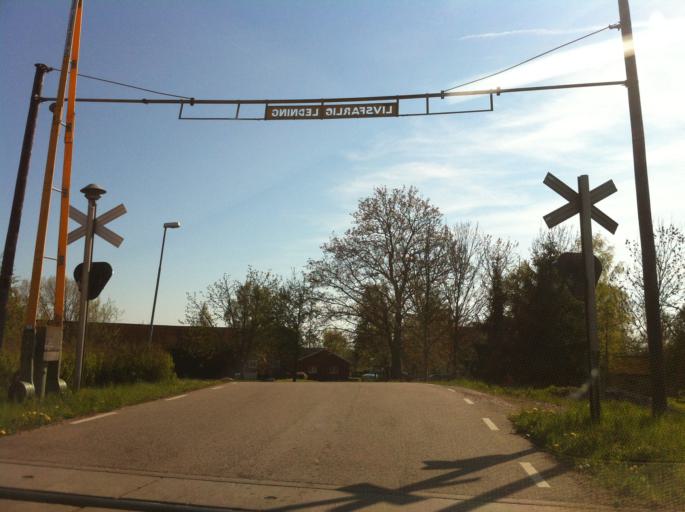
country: SE
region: Skane
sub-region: Svalovs Kommun
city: Kagerod
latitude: 55.9749
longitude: 13.0629
